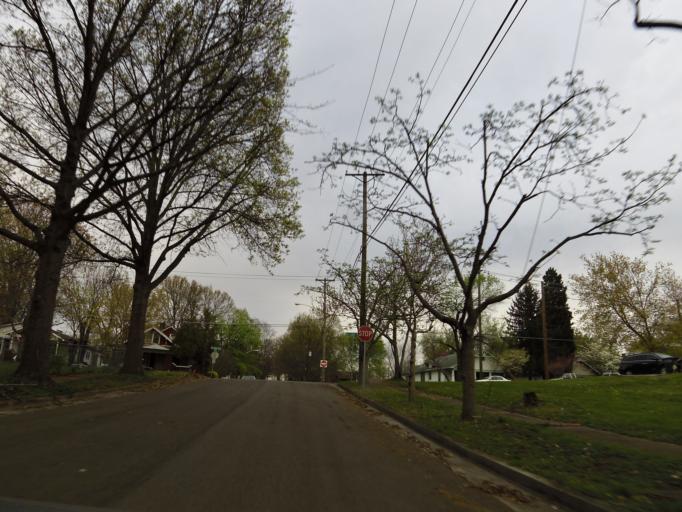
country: US
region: Tennessee
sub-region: Knox County
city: Knoxville
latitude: 35.9780
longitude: -83.9013
